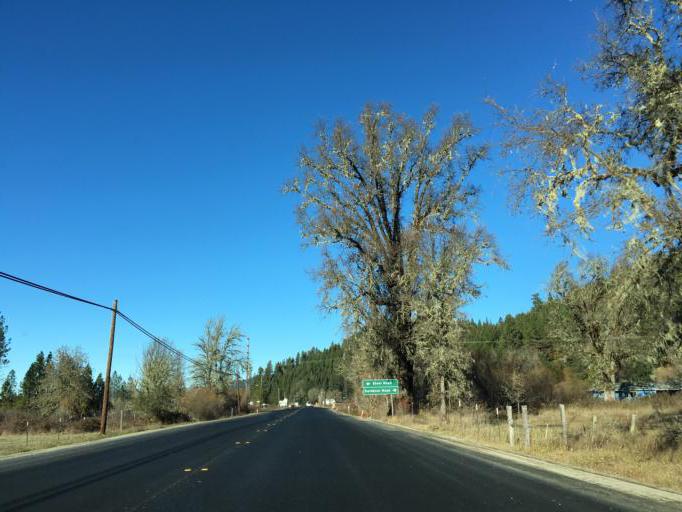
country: US
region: California
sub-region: Mendocino County
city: Laytonville
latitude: 39.6500
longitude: -123.4764
